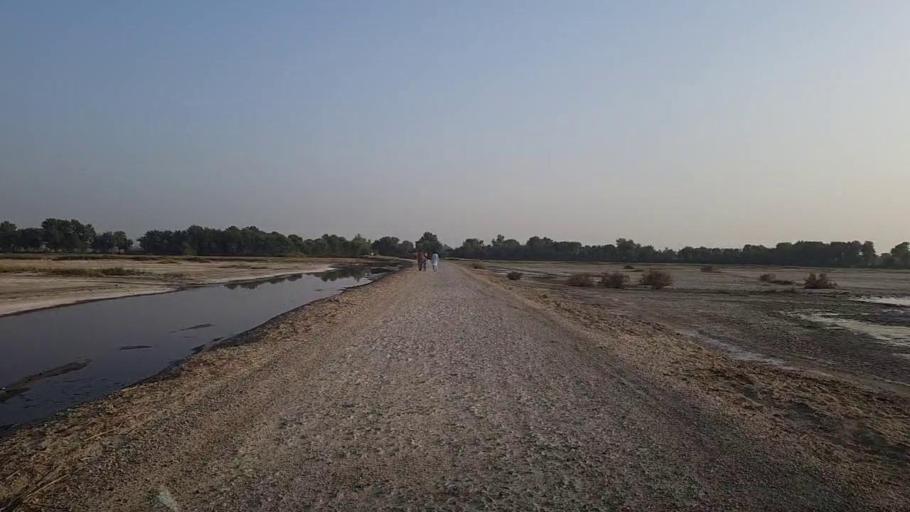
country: PK
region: Sindh
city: Kandhkot
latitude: 28.2440
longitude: 69.0914
